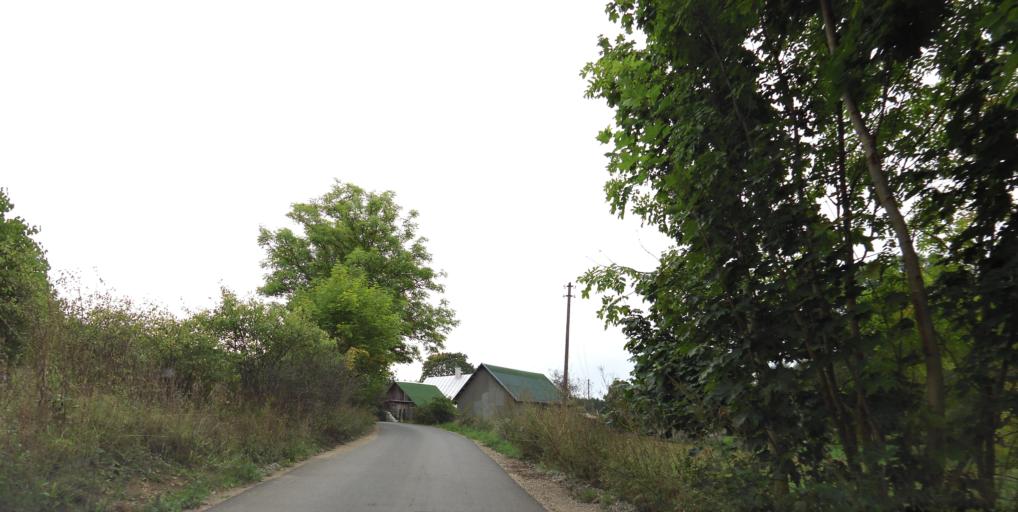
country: LT
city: Grigiskes
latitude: 54.7533
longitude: 25.0284
